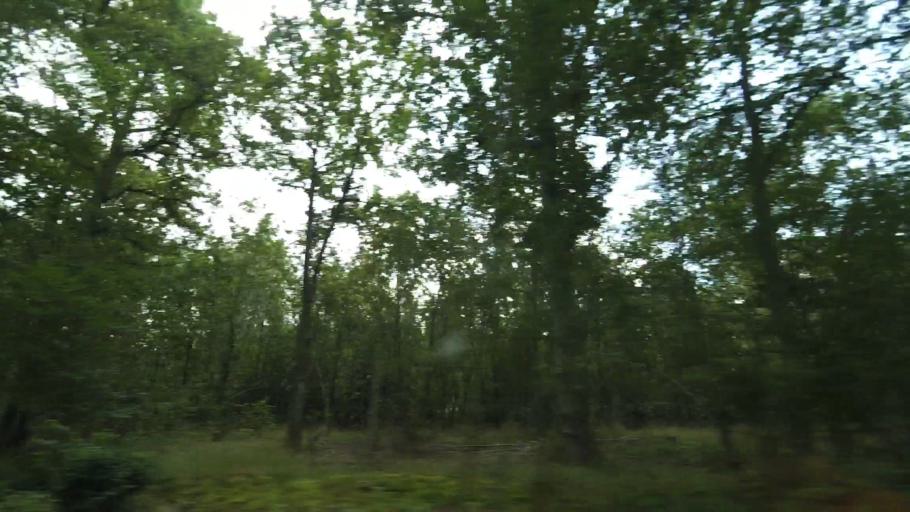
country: DK
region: Central Jutland
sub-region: Norddjurs Kommune
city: Allingabro
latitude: 56.4963
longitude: 10.3626
